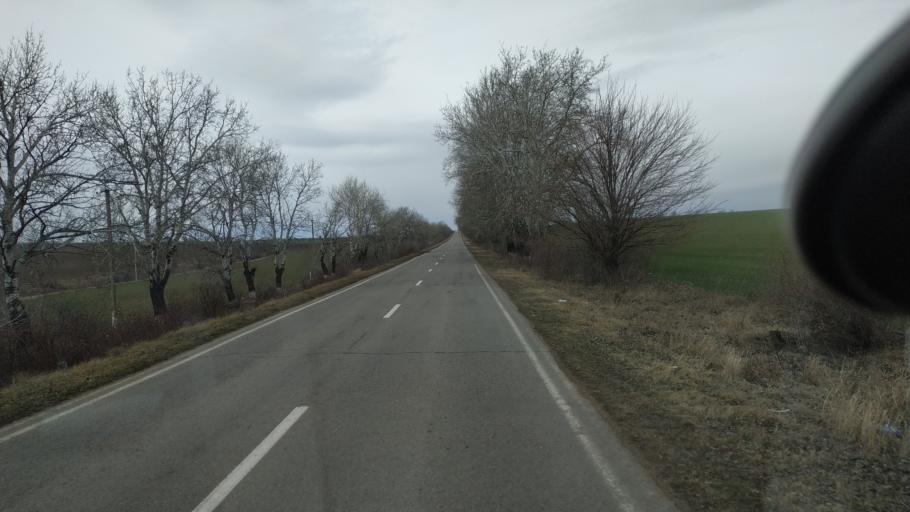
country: MD
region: Telenesti
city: Cocieri
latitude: 47.3671
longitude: 29.1133
